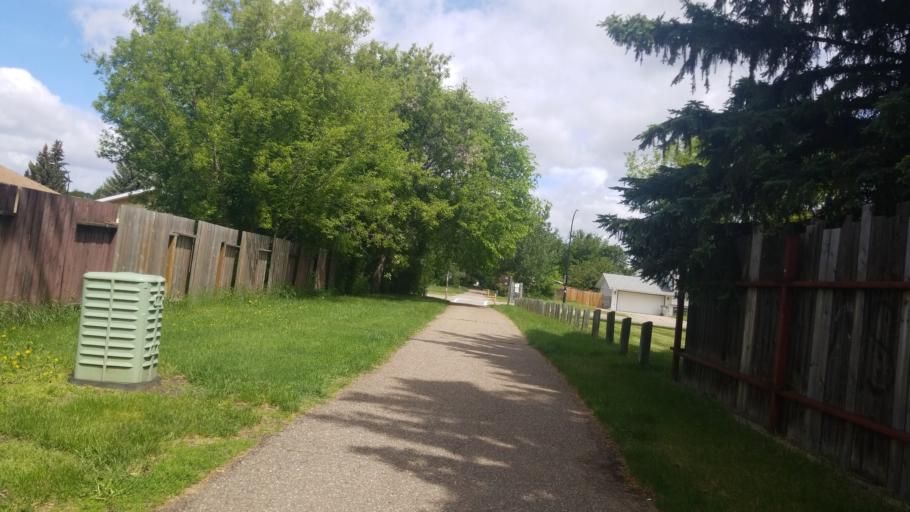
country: CA
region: Saskatchewan
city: Lloydminster
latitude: 53.2664
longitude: -110.0176
